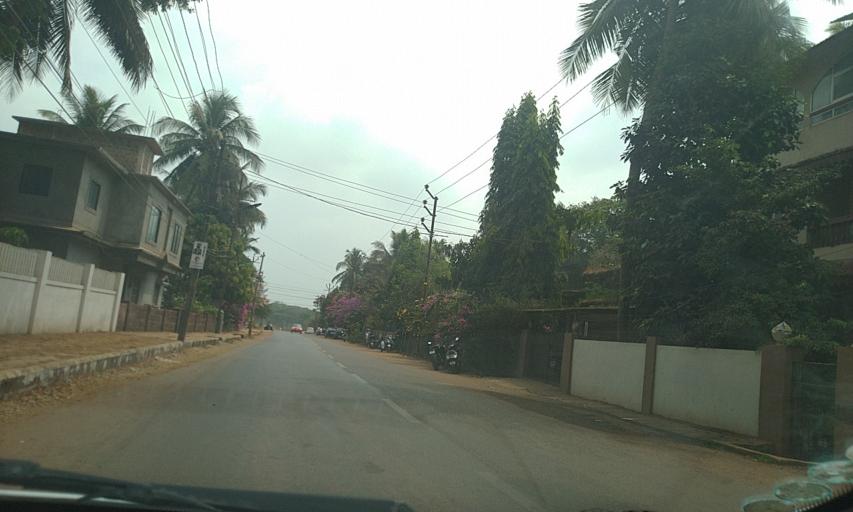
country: IN
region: Goa
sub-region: North Goa
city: Serula
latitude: 15.5361
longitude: 73.8268
